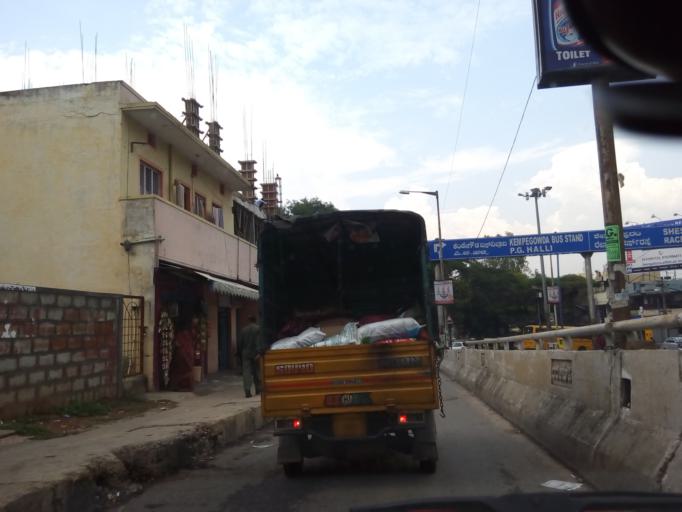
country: IN
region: Karnataka
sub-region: Bangalore Urban
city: Bangalore
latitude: 12.9969
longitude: 77.5725
